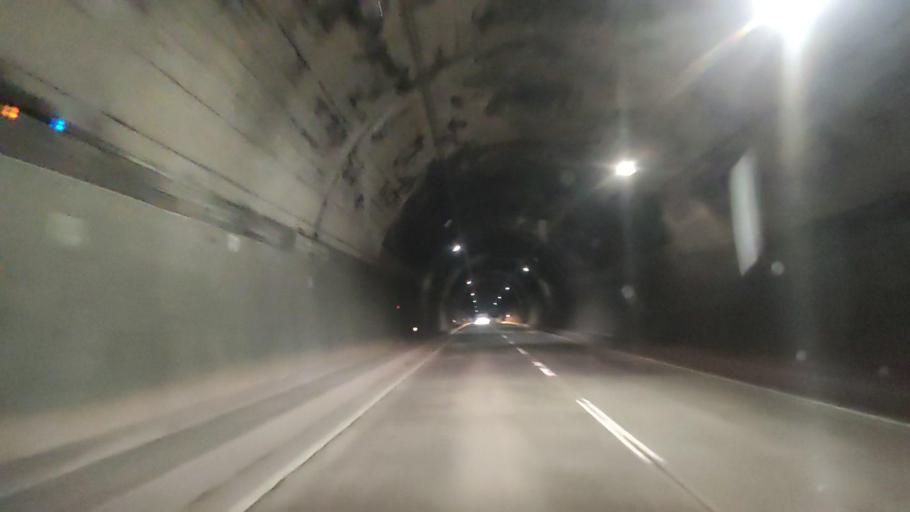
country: JP
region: Kagoshima
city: Okuchi-shinohara
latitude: 31.9755
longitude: 130.7413
